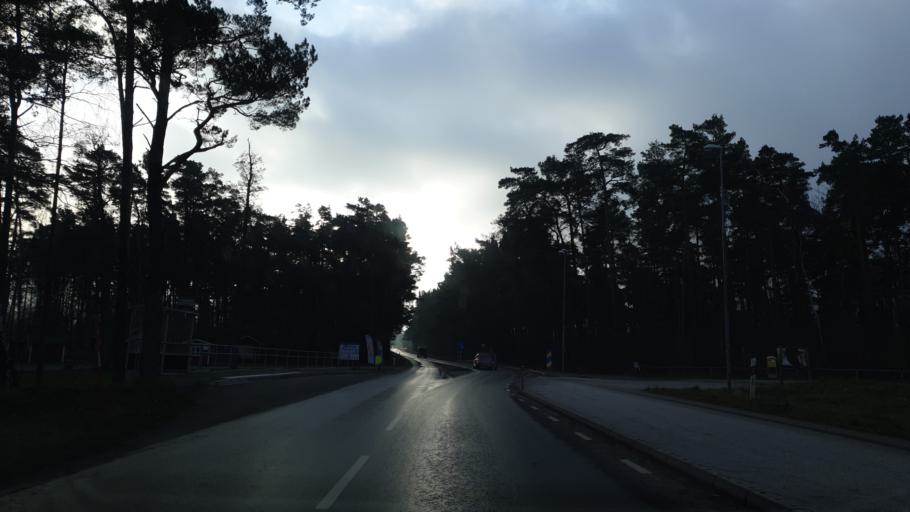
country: SE
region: Blekinge
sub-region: Karlshamns Kommun
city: Morrum
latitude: 56.1263
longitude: 14.6738
